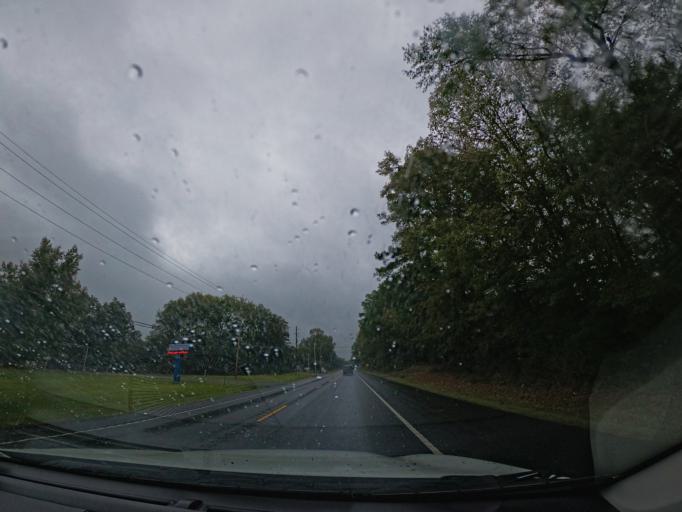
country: US
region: Louisiana
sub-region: Caddo Parish
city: Greenwood
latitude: 32.3770
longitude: -94.0312
